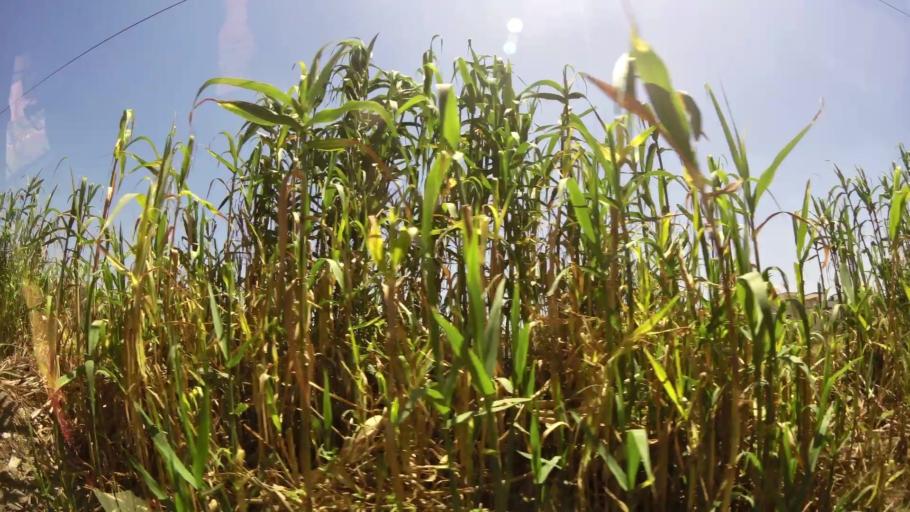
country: MA
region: Oriental
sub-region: Berkane-Taourirt
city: Madagh
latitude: 35.0741
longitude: -2.2161
